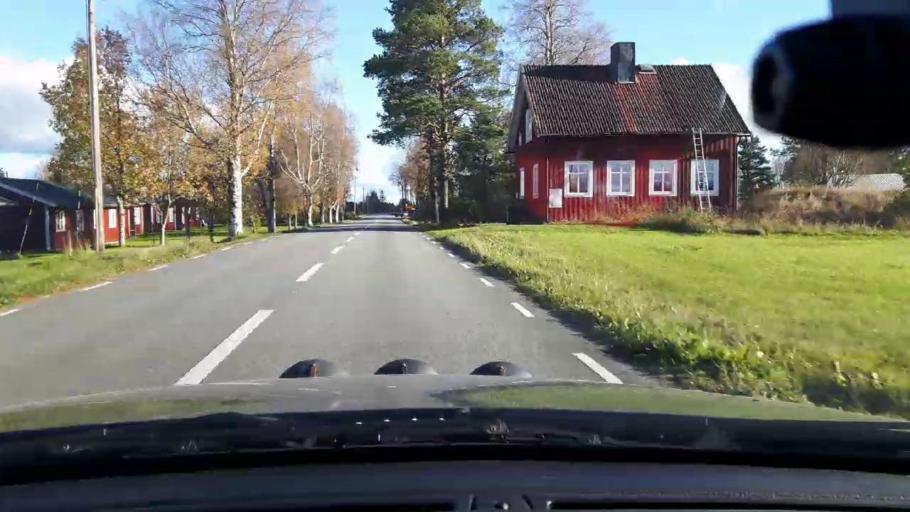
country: SE
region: Jaemtland
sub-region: Bergs Kommun
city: Hoverberg
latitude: 63.0690
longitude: 14.3190
